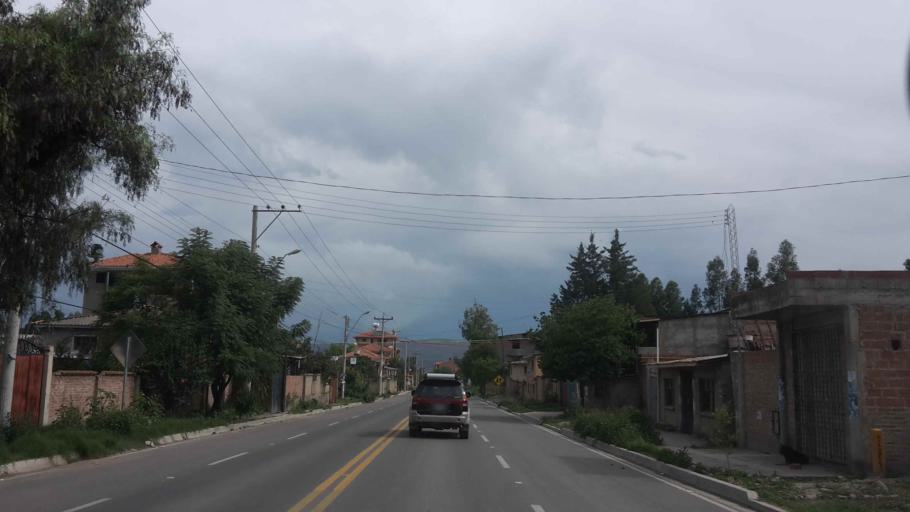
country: BO
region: Cochabamba
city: Cochabamba
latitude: -17.3648
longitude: -66.2526
